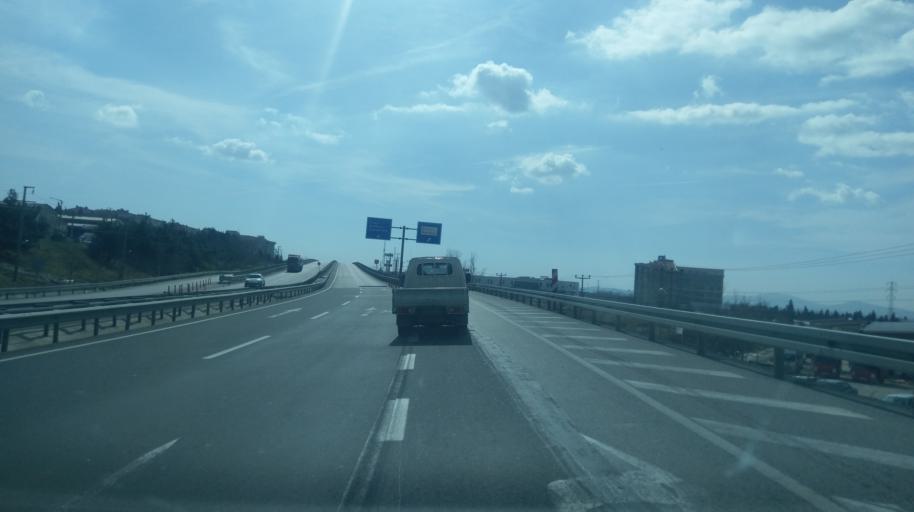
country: TR
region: Edirne
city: Kesan
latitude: 40.8623
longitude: 26.6217
